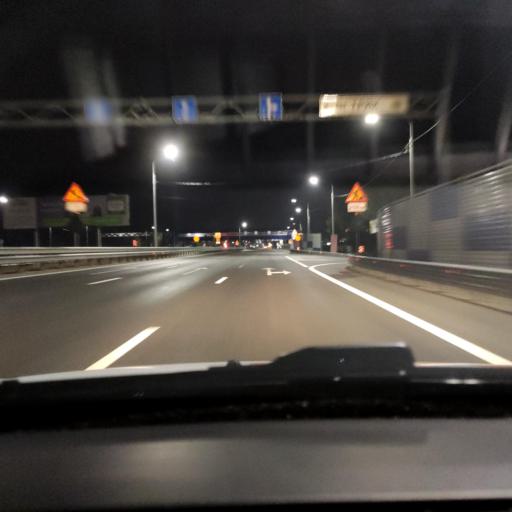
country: RU
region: Voronezj
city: Podgornoye
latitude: 51.7698
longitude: 39.1946
